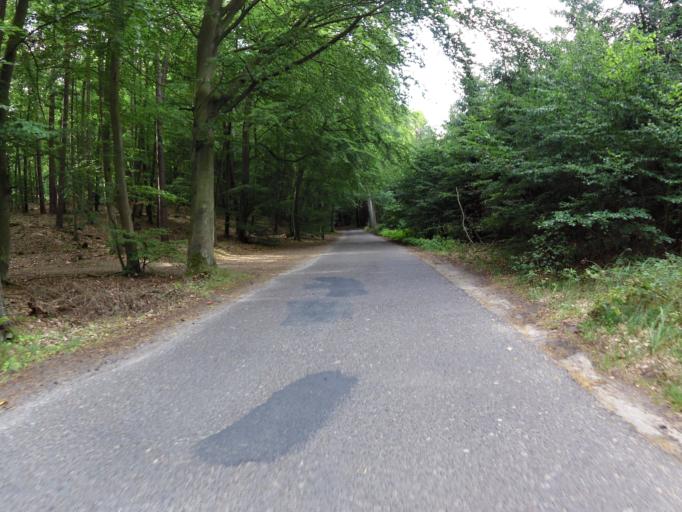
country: DE
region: Mecklenburg-Vorpommern
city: Seebad Bansin
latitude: 53.9803
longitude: 14.1087
